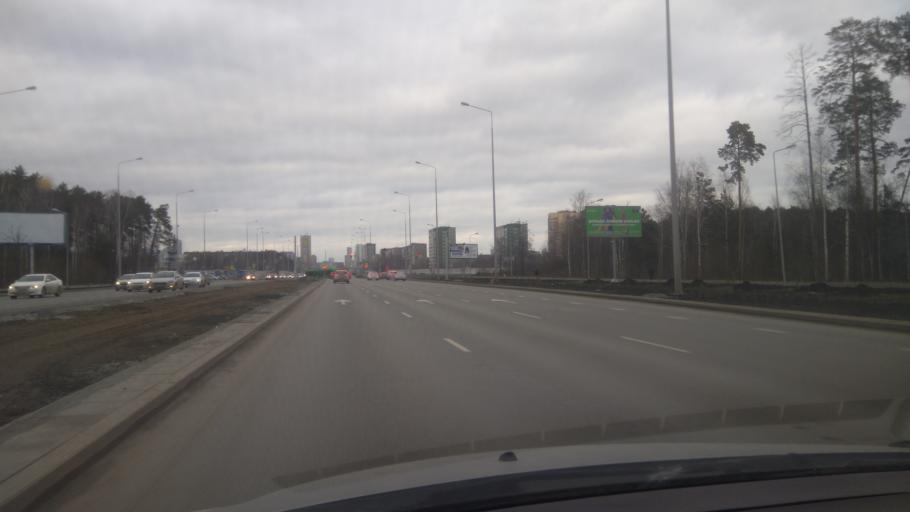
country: RU
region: Sverdlovsk
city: Sovkhoznyy
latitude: 56.8016
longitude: 60.5359
